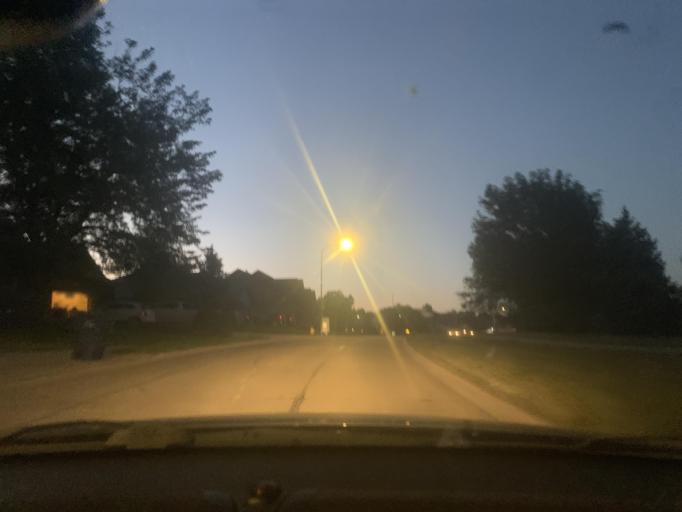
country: US
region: Nebraska
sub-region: Sarpy County
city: La Vista
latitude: 41.1786
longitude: -96.0562
